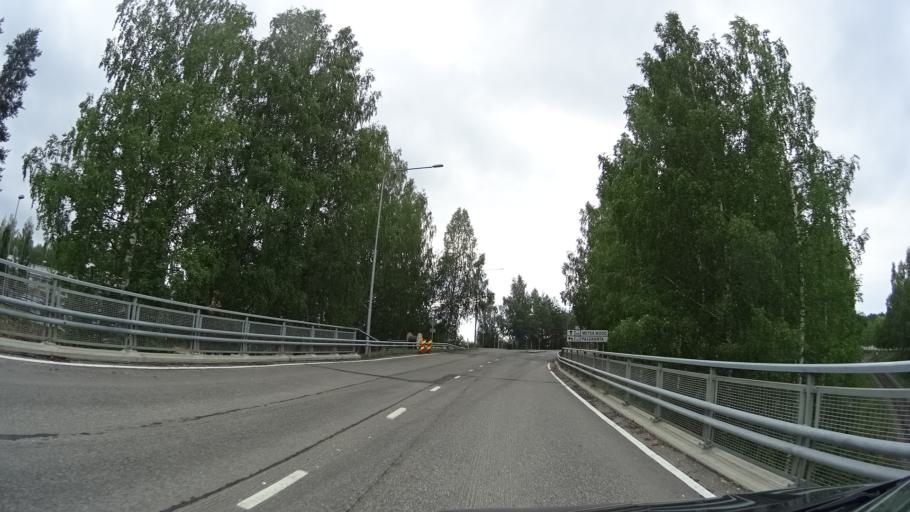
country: FI
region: Southern Savonia
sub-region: Savonlinna
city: Punkaharju
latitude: 61.7559
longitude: 29.3897
